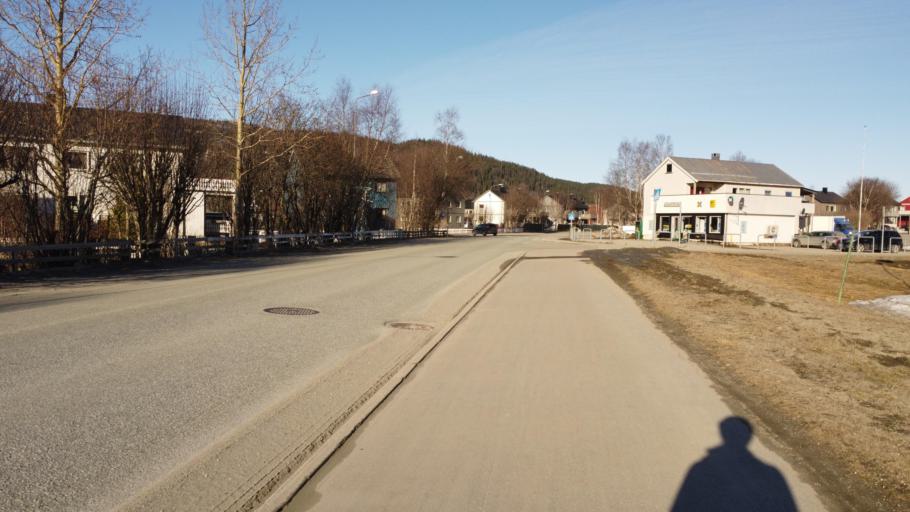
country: NO
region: Nordland
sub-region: Rana
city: Mo i Rana
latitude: 66.3191
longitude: 14.1831
